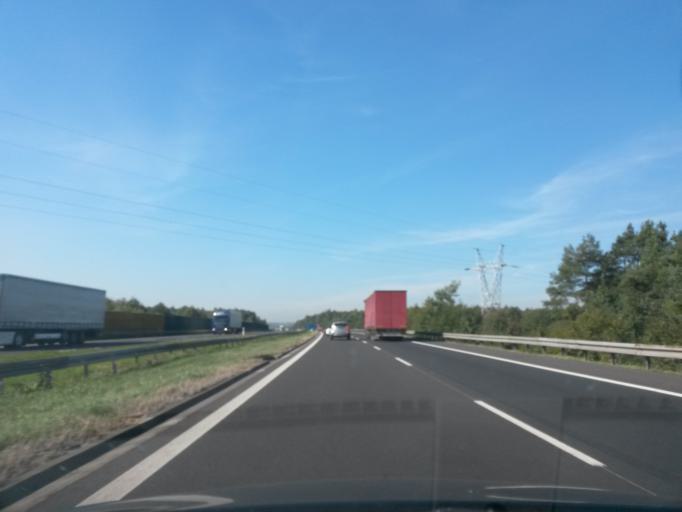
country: PL
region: Lesser Poland Voivodeship
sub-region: Powiat chrzanowski
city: Trzebinia
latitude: 50.1374
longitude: 19.4667
